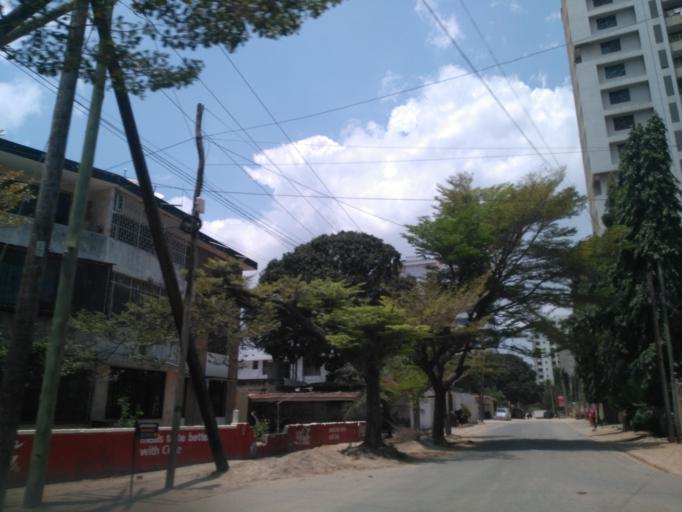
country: TZ
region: Dar es Salaam
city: Dar es Salaam
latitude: -6.8087
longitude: 39.2763
